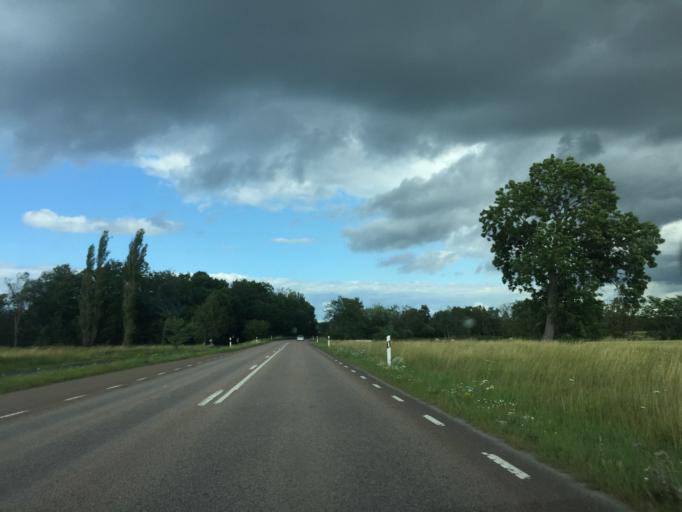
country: SE
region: OEstergoetland
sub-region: Vadstena Kommun
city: Vadstena
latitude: 58.4603
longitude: 14.9262
